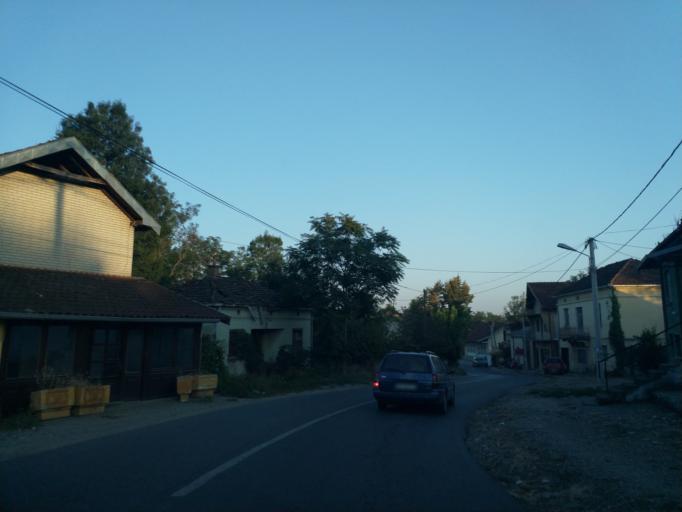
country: RS
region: Central Serbia
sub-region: Rasinski Okrug
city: Trstenik
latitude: 43.6318
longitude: 21.0751
